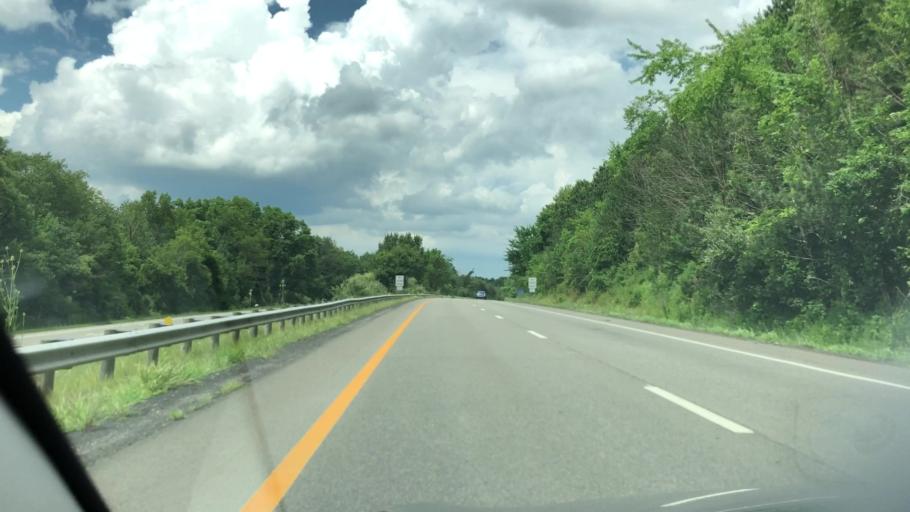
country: US
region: Ohio
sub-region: Summit County
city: Norton
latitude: 41.0716
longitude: -81.6649
